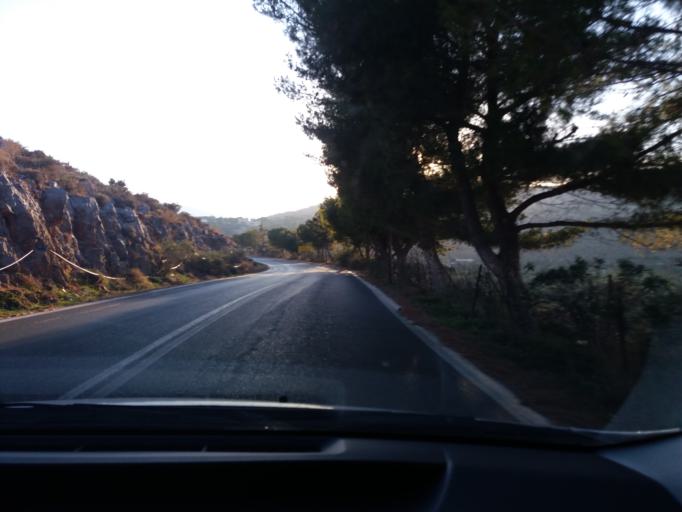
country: GR
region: Crete
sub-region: Nomos Irakleiou
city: Mokhos
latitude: 35.2708
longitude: 25.4263
